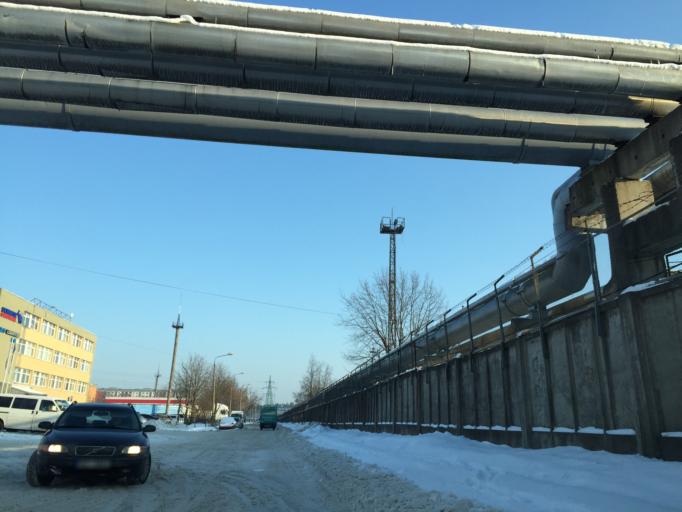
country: LV
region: Stopini
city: Ulbroka
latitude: 56.9290
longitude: 24.2064
